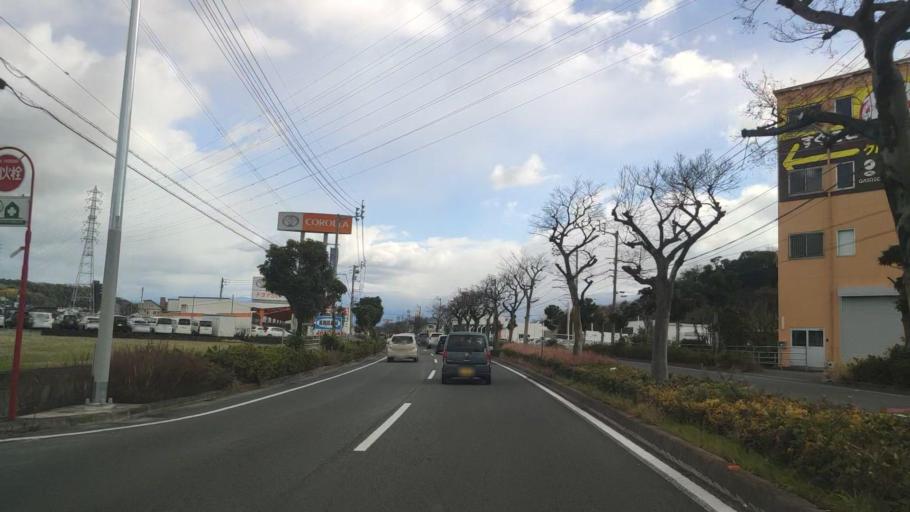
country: JP
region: Ehime
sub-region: Shikoku-chuo Shi
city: Matsuyama
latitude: 33.8208
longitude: 132.7880
